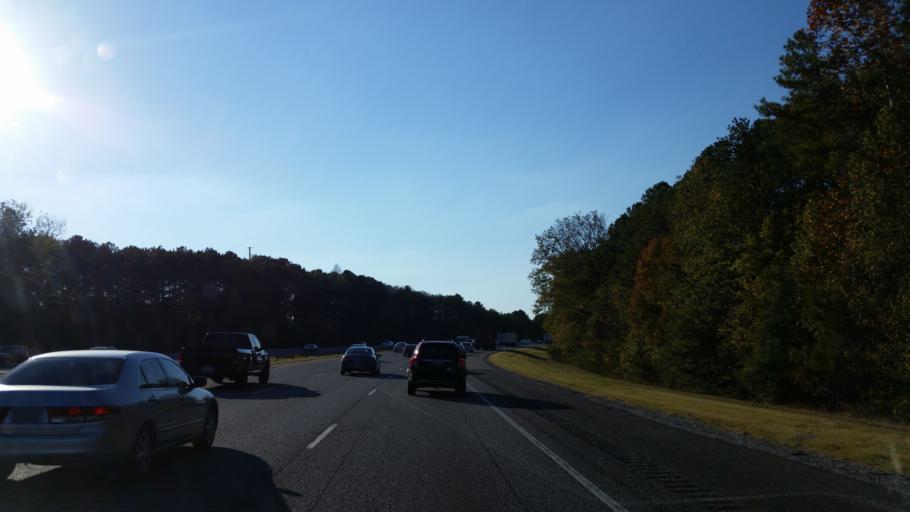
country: US
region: Georgia
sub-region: Cobb County
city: Acworth
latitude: 34.0884
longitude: -84.7174
